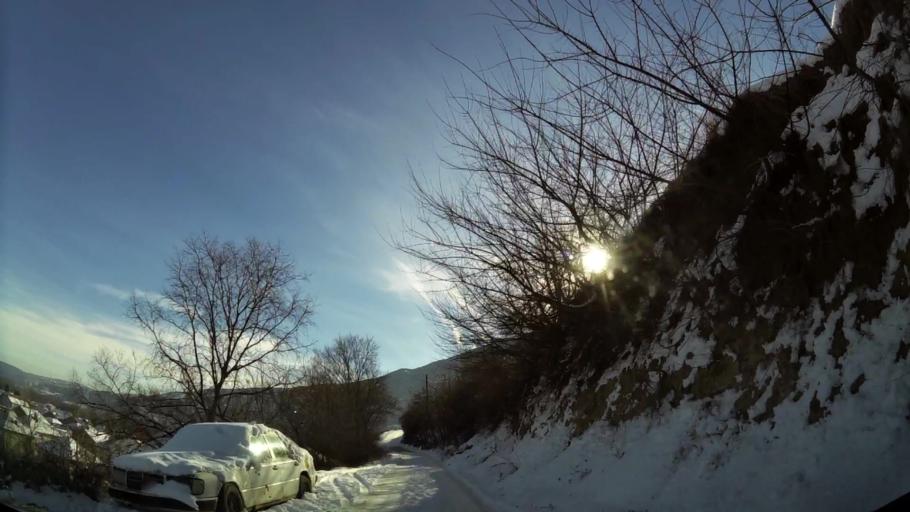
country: MK
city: Ljubin
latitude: 41.9804
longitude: 21.3022
